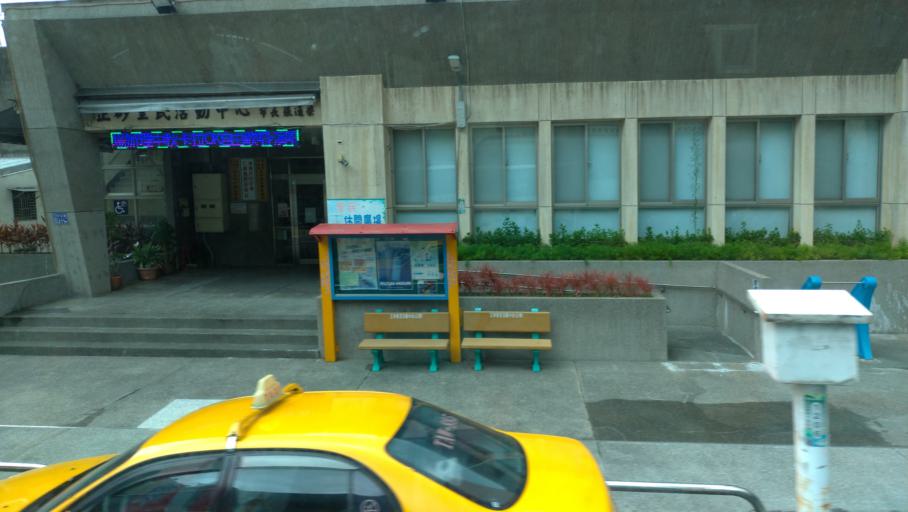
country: TW
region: Taiwan
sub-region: Keelung
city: Keelung
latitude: 25.1432
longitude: 121.7611
